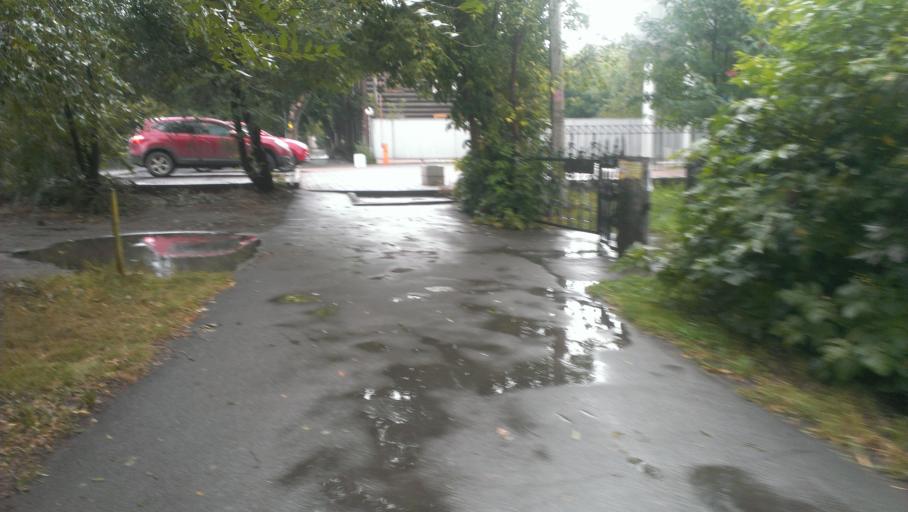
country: RU
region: Altai Krai
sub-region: Gorod Barnaulskiy
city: Barnaul
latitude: 53.3573
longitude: 83.7646
